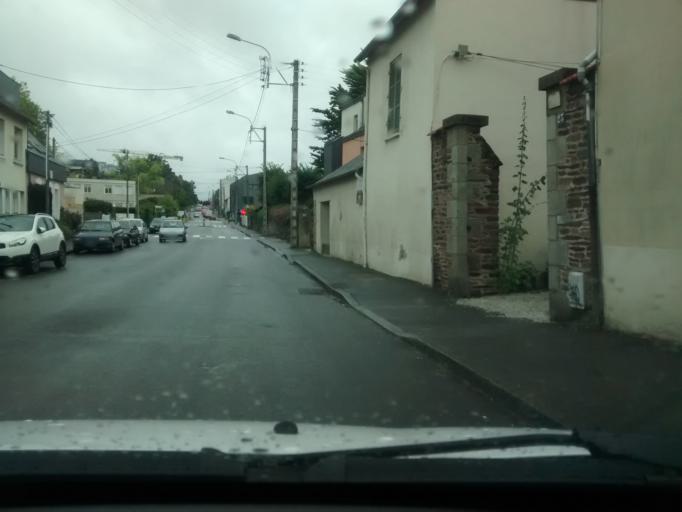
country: FR
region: Brittany
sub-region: Departement d'Ille-et-Vilaine
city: Rennes
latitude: 48.1267
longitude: -1.6697
